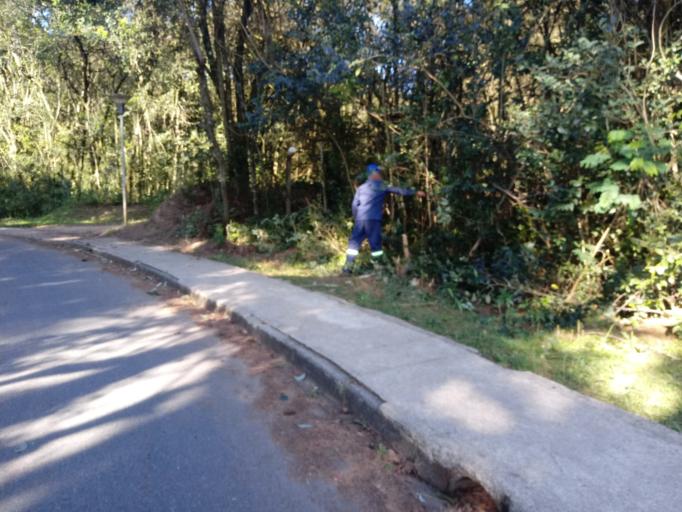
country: BR
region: Parana
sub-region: Curitiba
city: Curitiba
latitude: -25.4503
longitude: -49.2390
